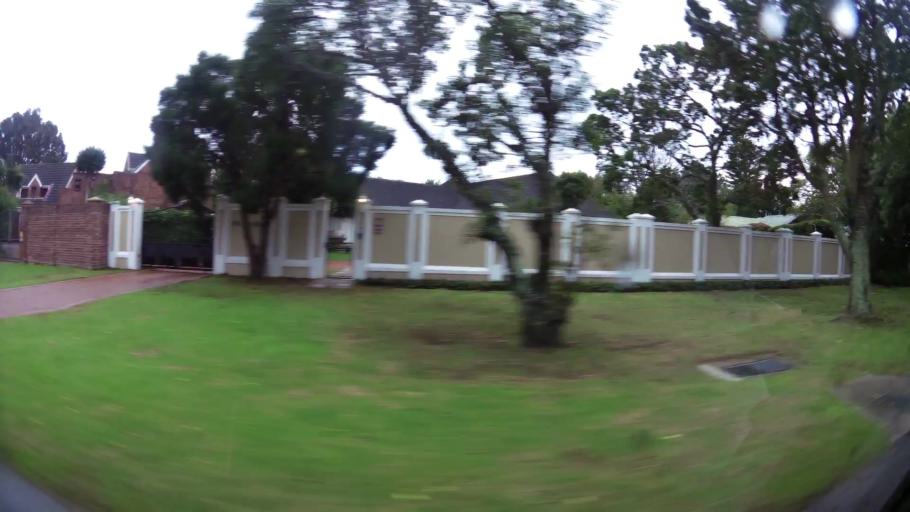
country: ZA
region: Eastern Cape
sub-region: Nelson Mandela Bay Metropolitan Municipality
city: Port Elizabeth
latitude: -33.9775
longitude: 25.5747
